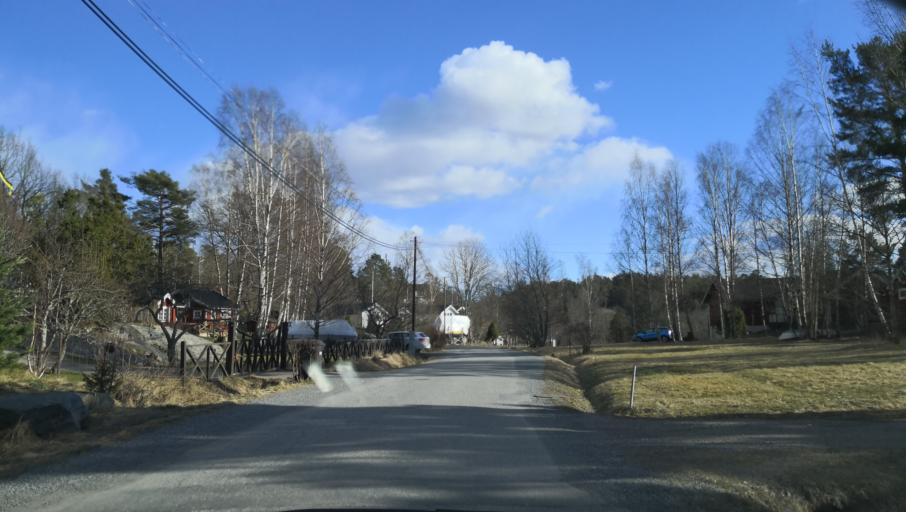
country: SE
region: Stockholm
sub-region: Varmdo Kommun
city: Hemmesta
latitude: 59.2438
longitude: 18.5105
